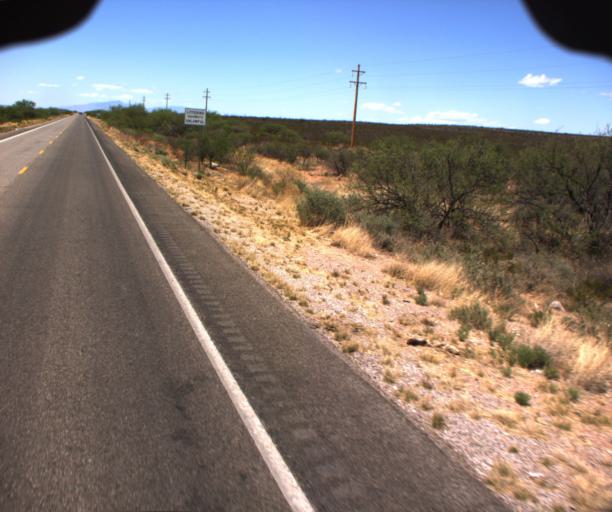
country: US
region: Arizona
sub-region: Cochise County
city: Tombstone
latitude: 31.7566
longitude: -110.1066
